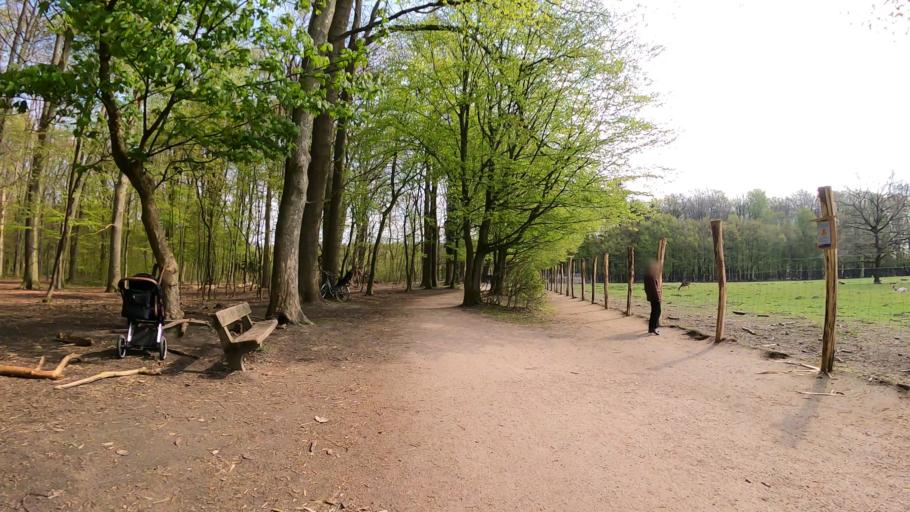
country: DE
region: Hamburg
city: Stellingen
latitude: 53.6139
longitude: 9.9379
